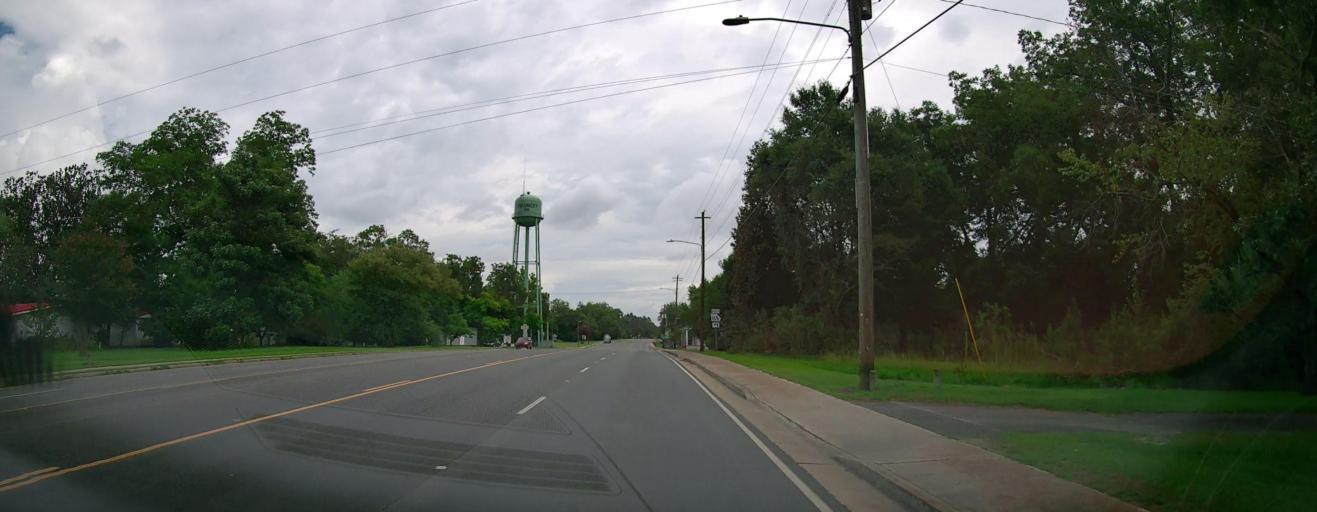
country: US
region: Georgia
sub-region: Dodge County
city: Eastman
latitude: 32.1051
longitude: -83.0679
